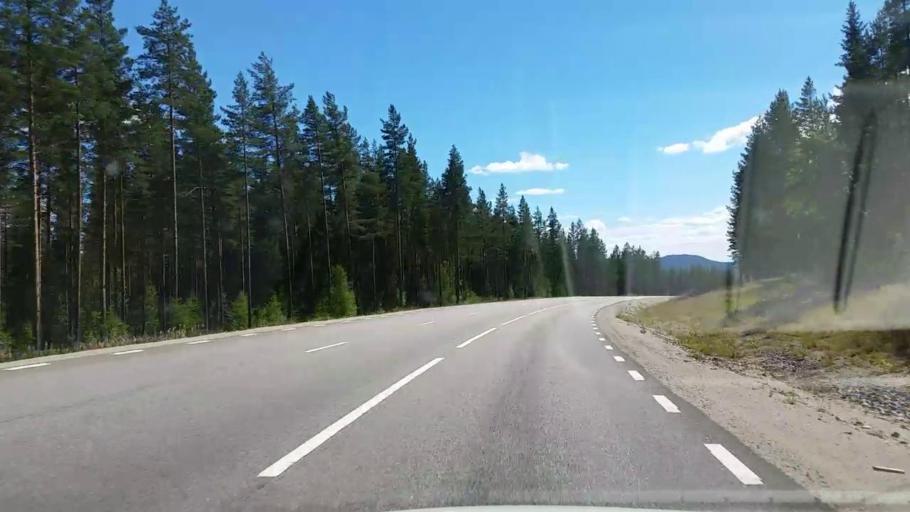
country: SE
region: Gaevleborg
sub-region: Bollnas Kommun
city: Vittsjo
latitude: 61.0594
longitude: 15.8034
